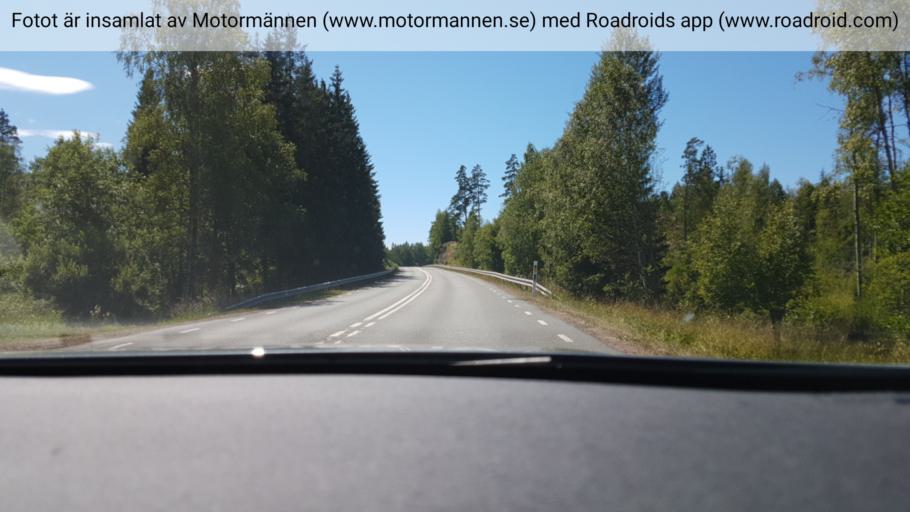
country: SE
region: Joenkoeping
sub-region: Jonkopings Kommun
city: Asa
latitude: 58.0113
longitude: 14.6452
